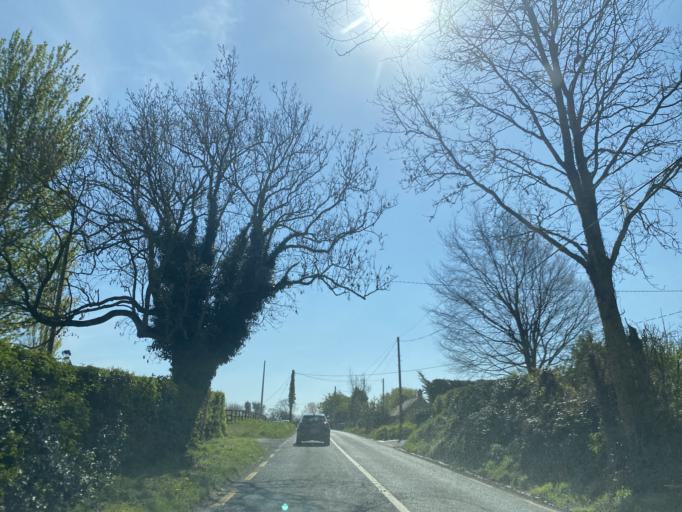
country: IE
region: Leinster
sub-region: Kildare
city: Kill
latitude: 53.2882
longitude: -6.6064
